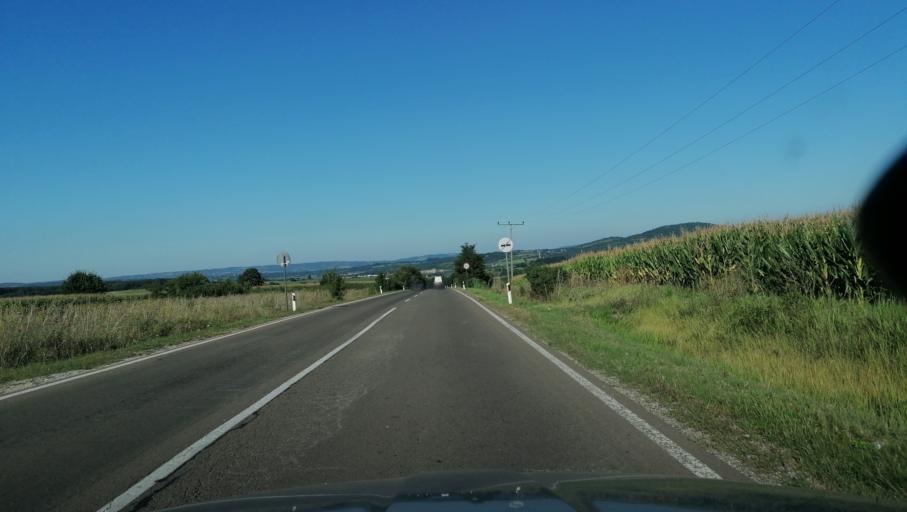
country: RS
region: Central Serbia
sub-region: Sumadijski Okrug
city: Knic
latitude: 43.9143
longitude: 20.6449
